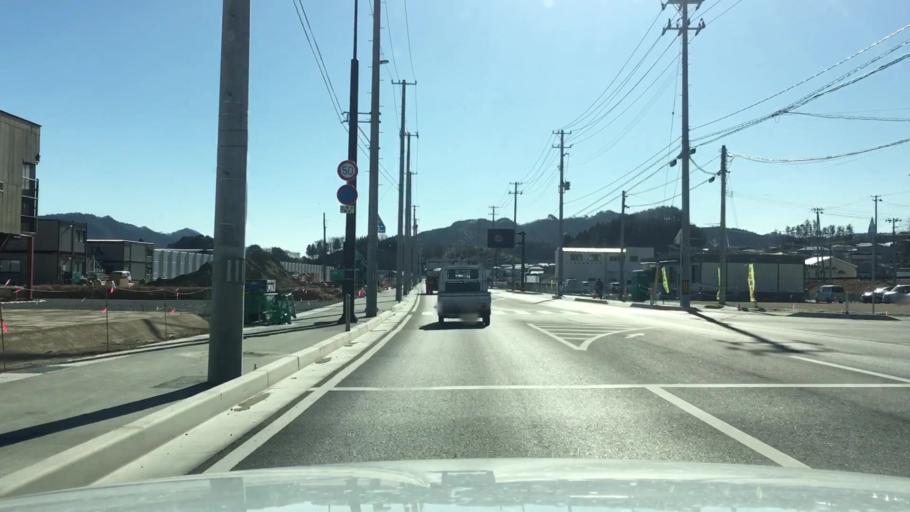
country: JP
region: Iwate
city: Yamada
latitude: 39.4648
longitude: 141.9529
